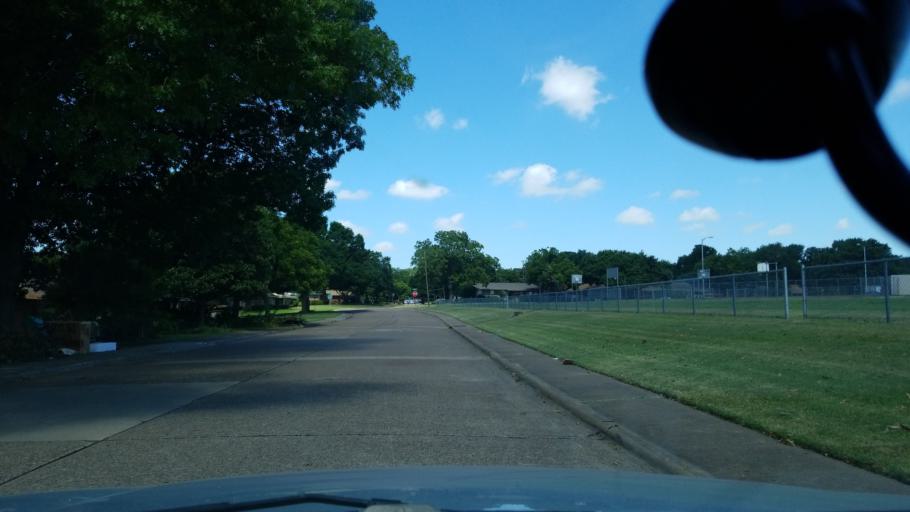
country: US
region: Texas
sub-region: Dallas County
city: Cockrell Hill
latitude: 32.6830
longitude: -96.8330
